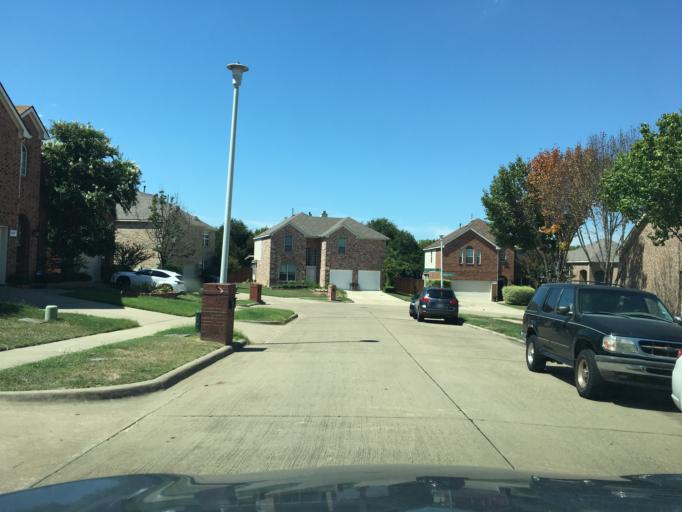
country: US
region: Texas
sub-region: Dallas County
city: Garland
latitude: 32.9509
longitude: -96.6443
